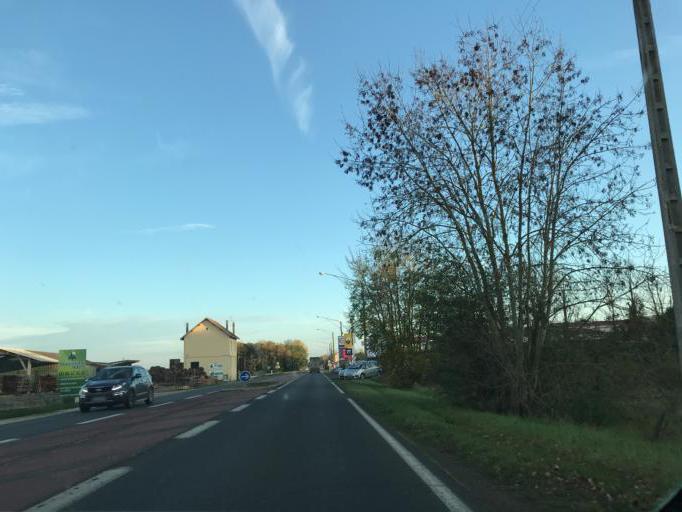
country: FR
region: Bourgogne
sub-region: Departement de l'Yonne
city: Pont-sur-Yonne
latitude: 48.2827
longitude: 3.2138
